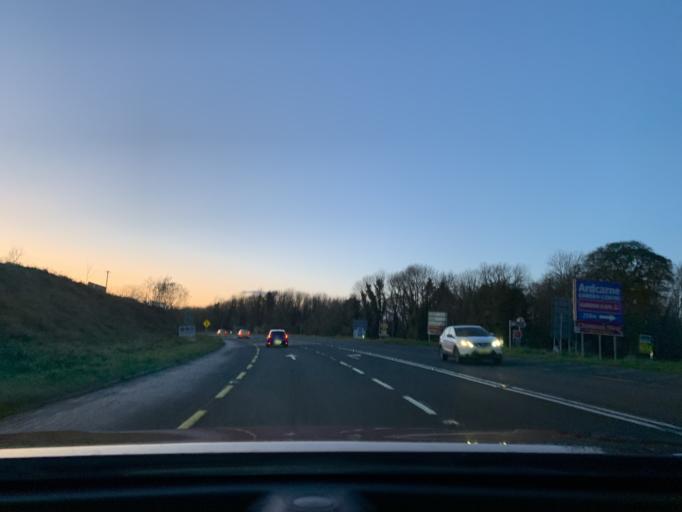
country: IE
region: Connaught
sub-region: Roscommon
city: Boyle
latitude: 53.9702
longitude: -8.2044
